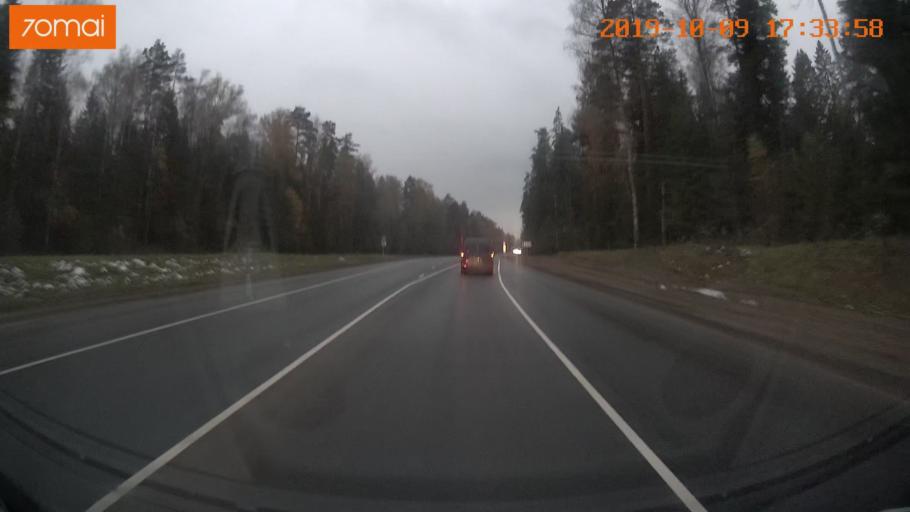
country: RU
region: Ivanovo
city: Bogorodskoye
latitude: 57.1112
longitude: 41.0163
